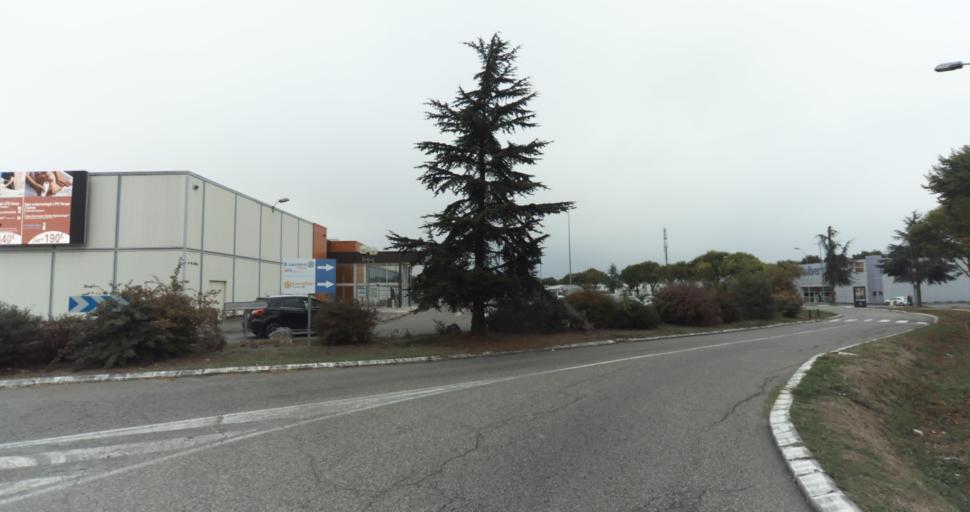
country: FR
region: Midi-Pyrenees
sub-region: Departement du Gers
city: Auch
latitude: 43.6657
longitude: 0.5929
